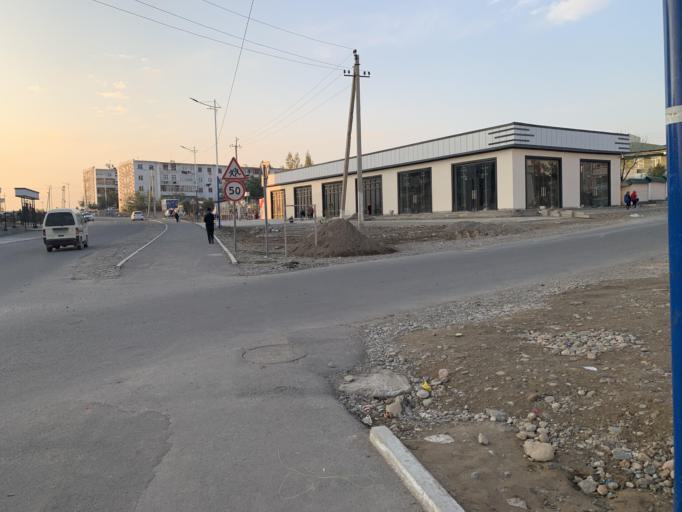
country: UZ
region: Namangan
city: Namangan Shahri
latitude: 41.0022
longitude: 71.5988
